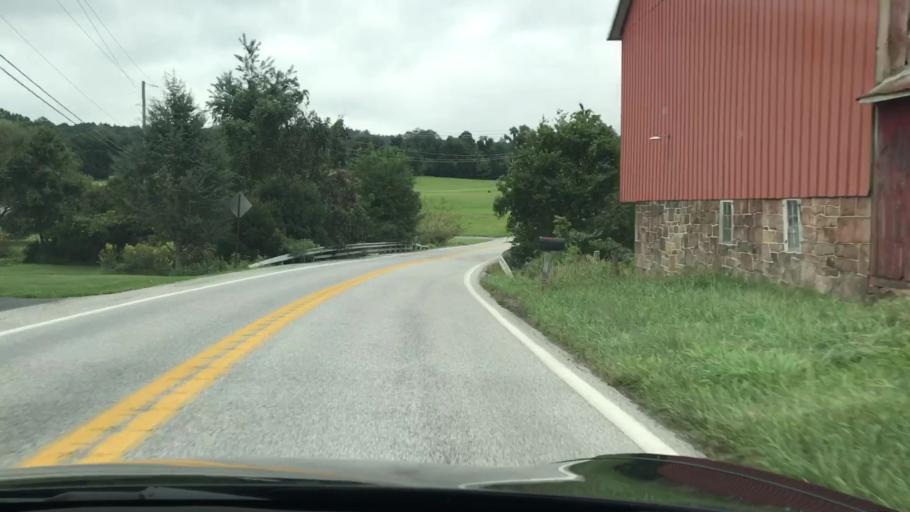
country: US
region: Pennsylvania
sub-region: York County
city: Dillsburg
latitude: 40.1263
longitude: -76.9600
